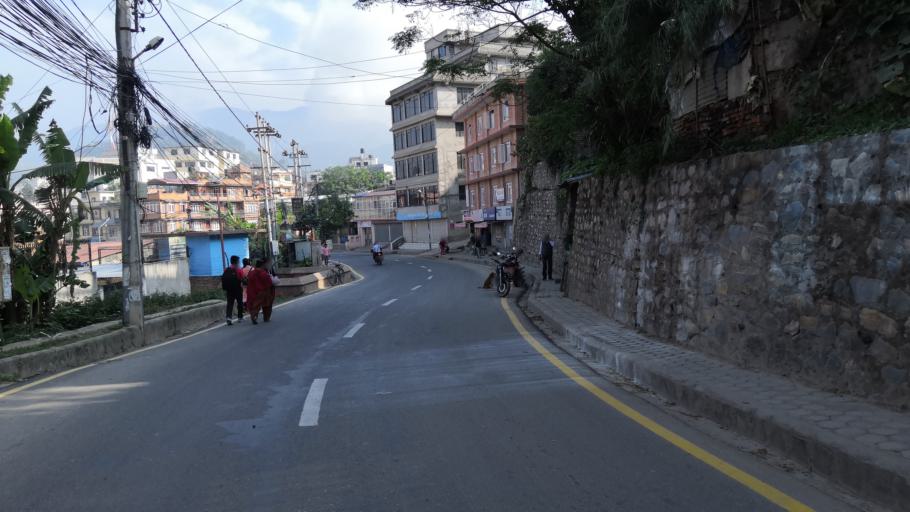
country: NP
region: Central Region
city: Kirtipur
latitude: 27.7070
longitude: 85.2855
